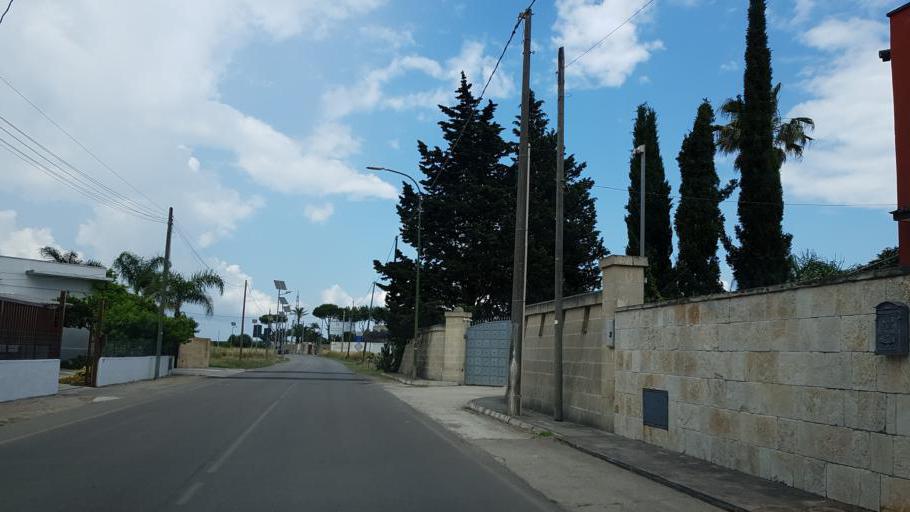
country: IT
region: Apulia
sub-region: Provincia di Brindisi
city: San Donaci
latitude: 40.4559
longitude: 17.9224
